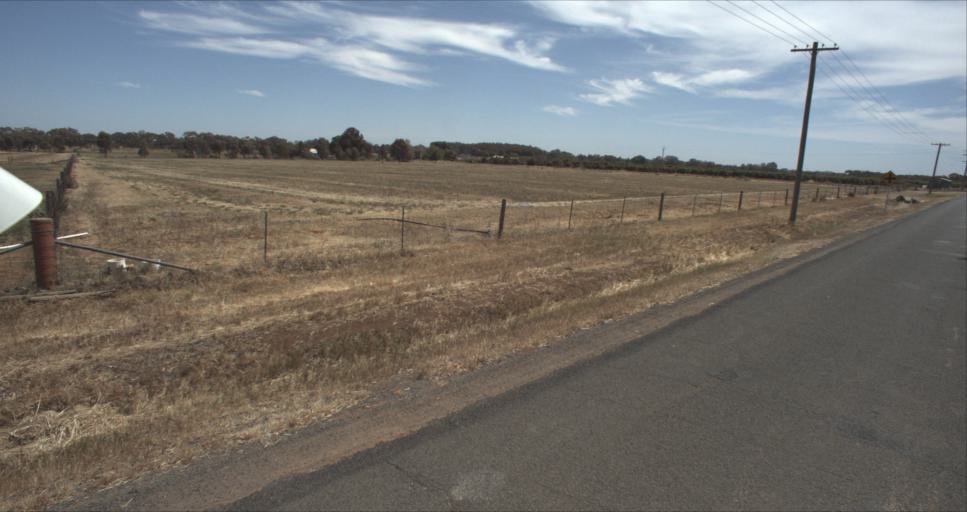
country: AU
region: New South Wales
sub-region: Leeton
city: Leeton
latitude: -34.5875
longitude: 146.4277
